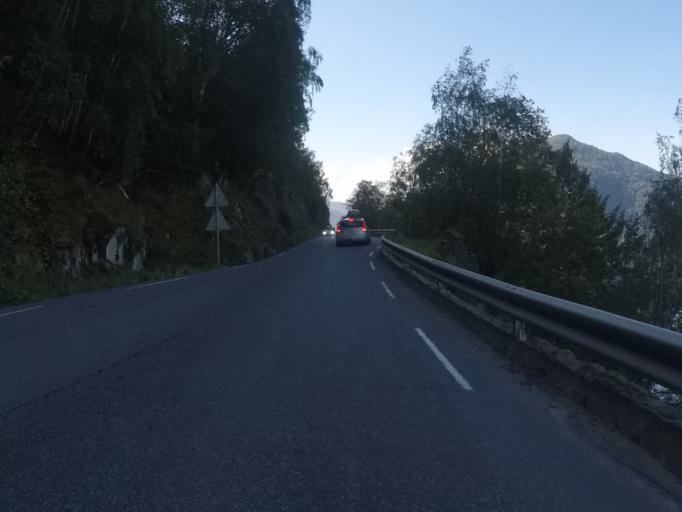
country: NO
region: Sogn og Fjordane
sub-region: Vik
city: Vikoyri
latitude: 61.1152
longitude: 6.6005
